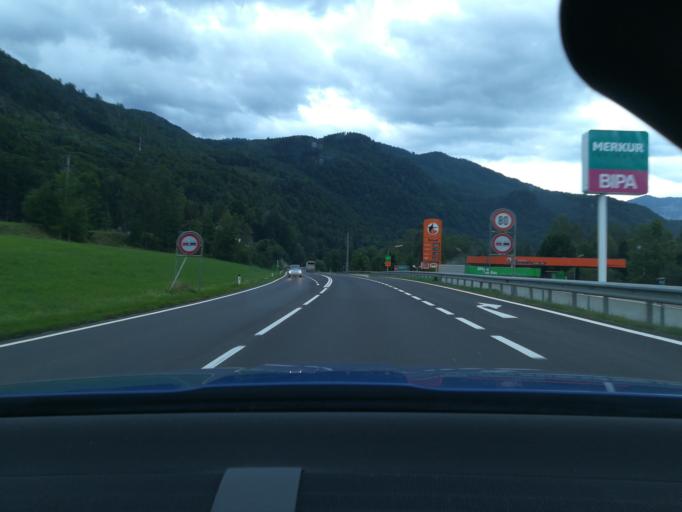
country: AT
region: Upper Austria
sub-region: Politischer Bezirk Gmunden
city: Bad Ischl
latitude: 47.6901
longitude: 13.6242
